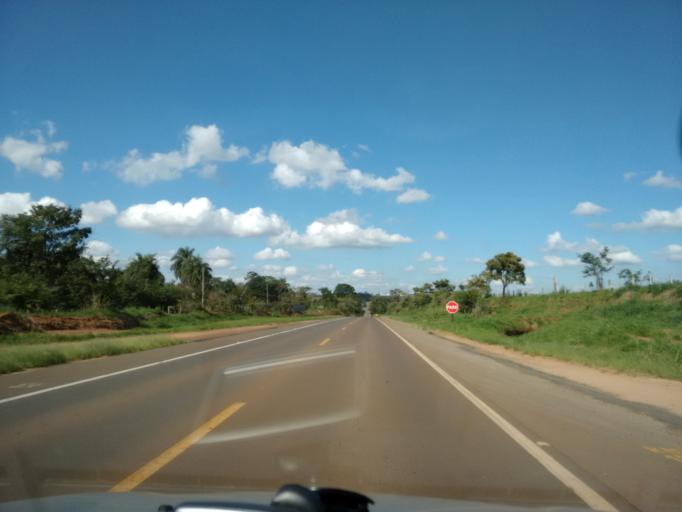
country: BR
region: Sao Paulo
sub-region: Sao Carlos
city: Sao Carlos
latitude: -22.0652
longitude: -47.9231
